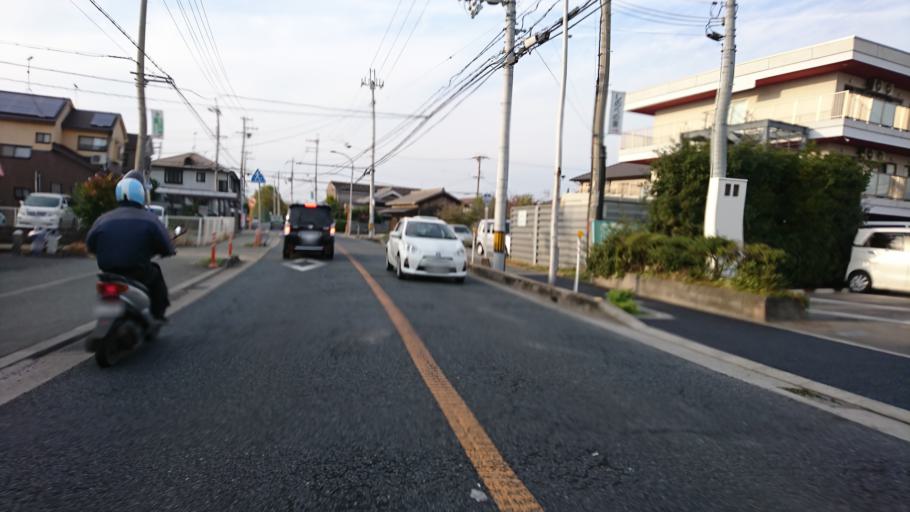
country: JP
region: Hyogo
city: Kakogawacho-honmachi
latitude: 34.7292
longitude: 134.8397
